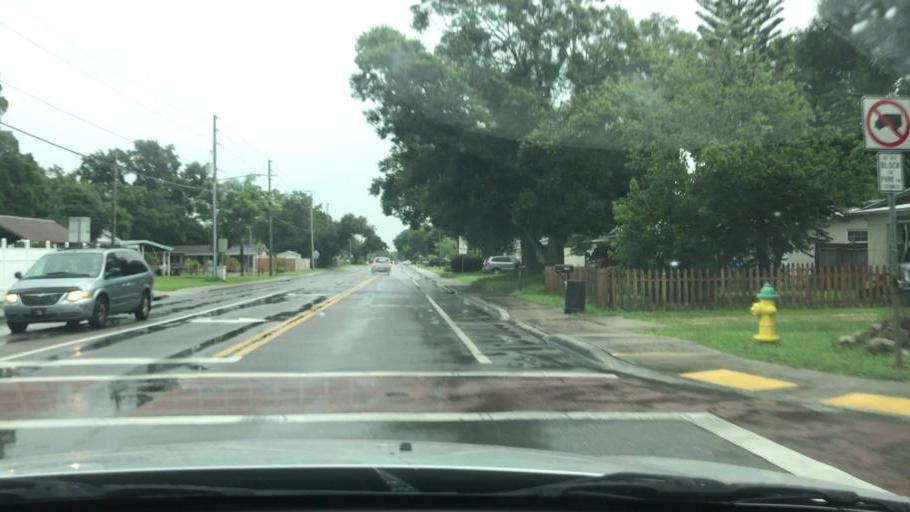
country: US
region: Florida
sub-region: Pinellas County
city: Pinellas Park
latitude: 27.8574
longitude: -82.7124
